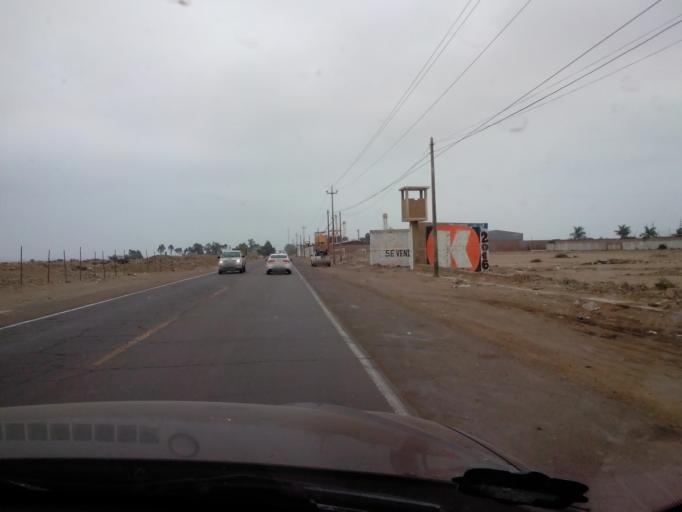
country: PE
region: Ica
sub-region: Provincia de Chincha
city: San Pedro
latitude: -13.4107
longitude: -76.1735
